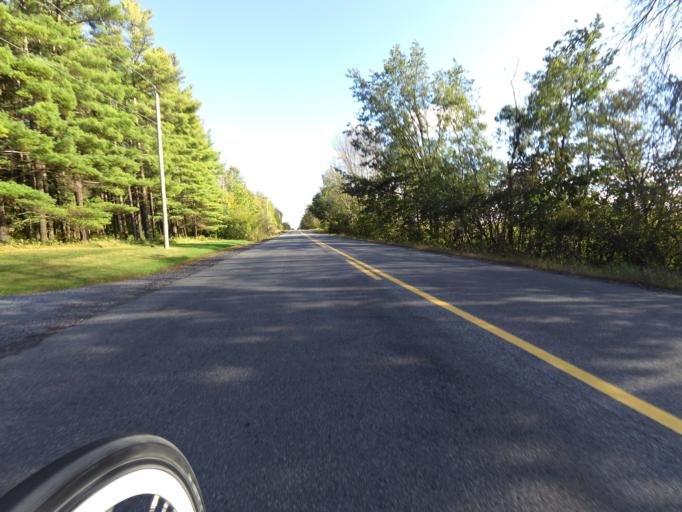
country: CA
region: Ontario
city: Bells Corners
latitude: 45.1313
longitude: -75.7503
